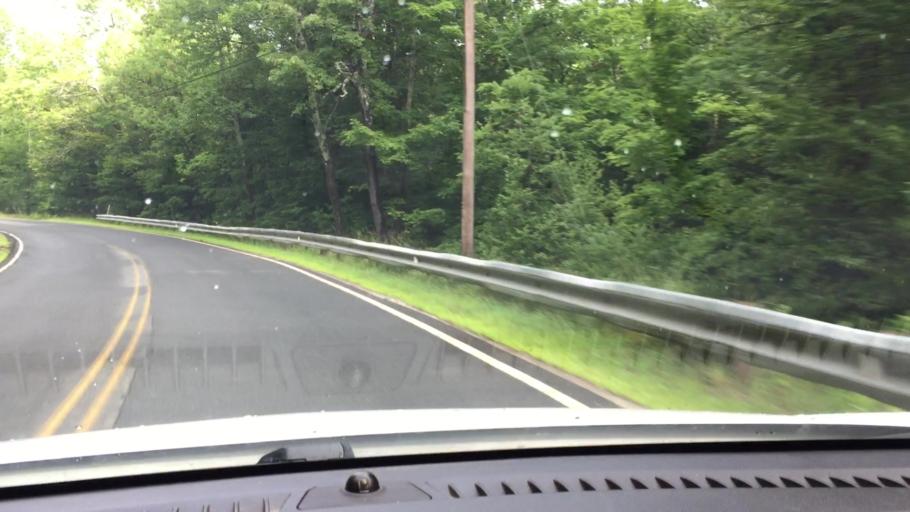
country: US
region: Massachusetts
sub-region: Berkshire County
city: Becket
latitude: 42.4269
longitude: -72.9956
